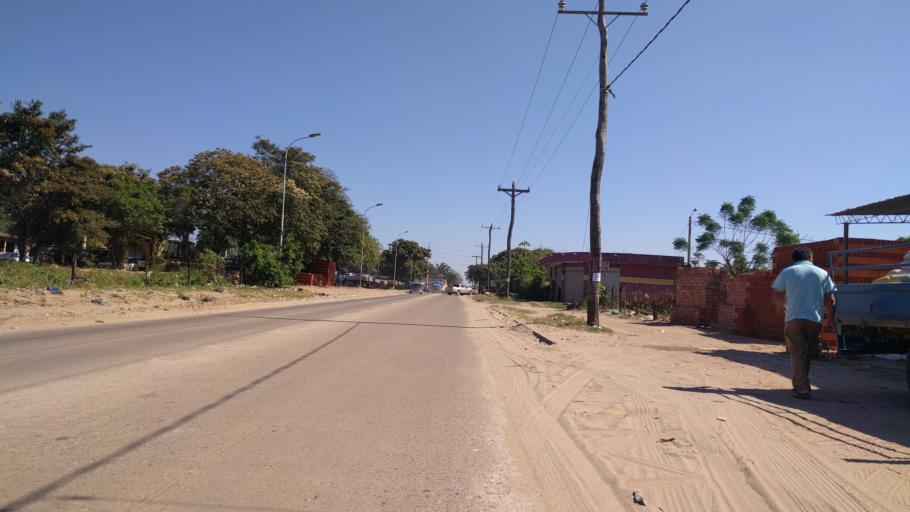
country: BO
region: Santa Cruz
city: Santa Cruz de la Sierra
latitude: -17.8444
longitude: -63.2119
